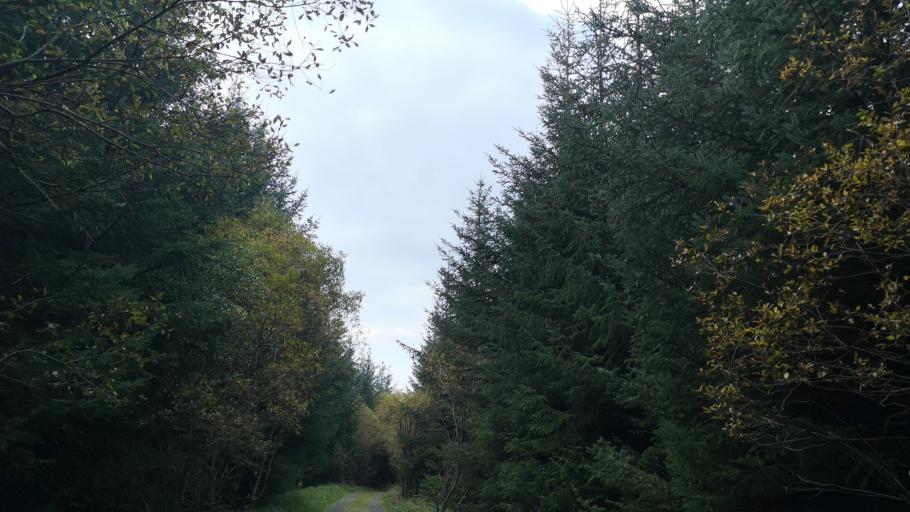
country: IE
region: Connaught
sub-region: County Galway
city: Loughrea
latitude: 53.2383
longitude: -8.6457
